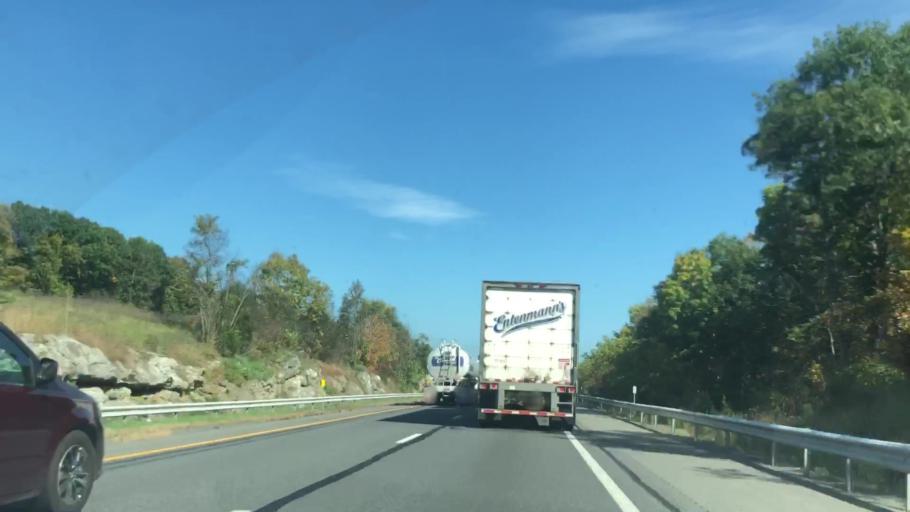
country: US
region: New York
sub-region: Greene County
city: Coxsackie
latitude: 42.3454
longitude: -73.8564
